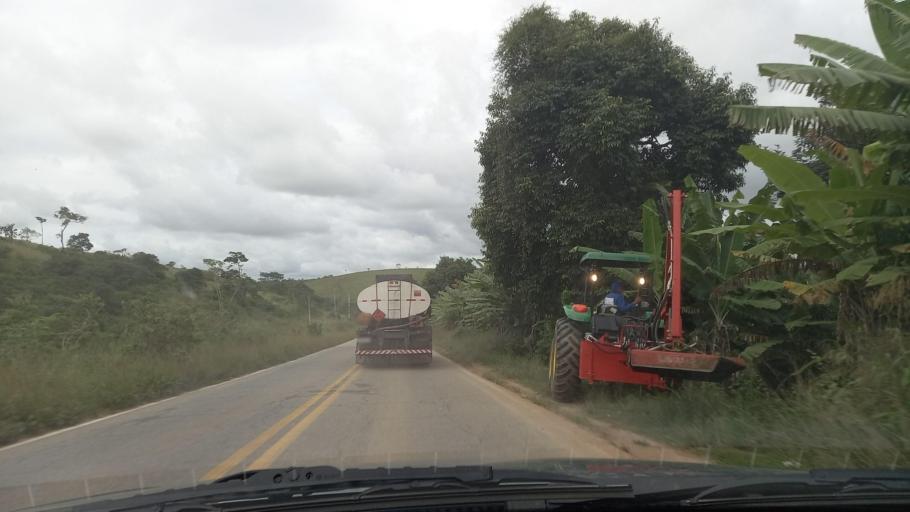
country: BR
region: Pernambuco
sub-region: Canhotinho
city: Canhotinho
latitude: -8.8720
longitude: -36.1982
